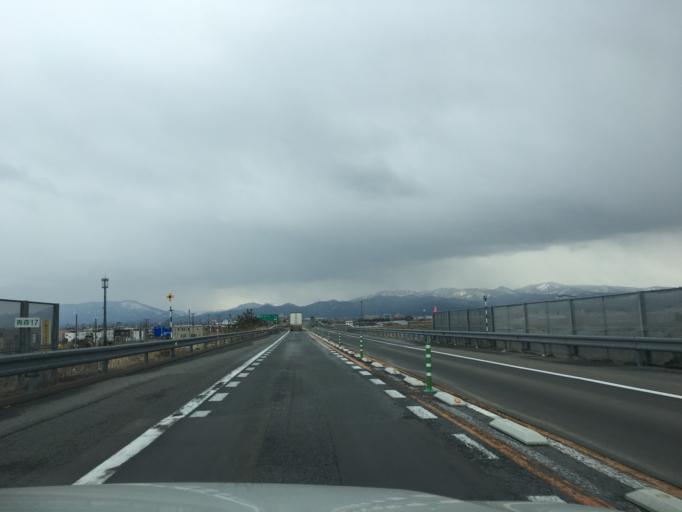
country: JP
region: Aomori
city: Aomori Shi
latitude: 40.7977
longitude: 140.7162
